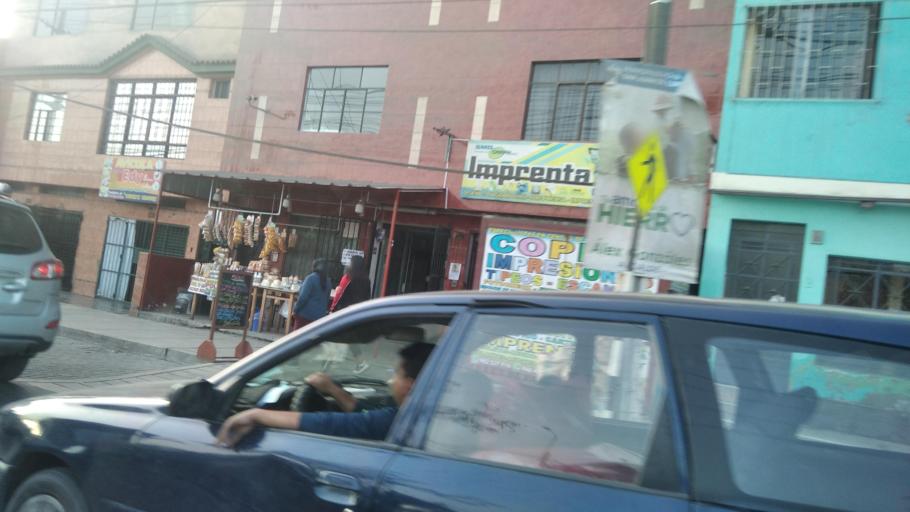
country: PE
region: Lima
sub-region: Lima
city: Vitarte
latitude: -12.0241
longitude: -76.9771
